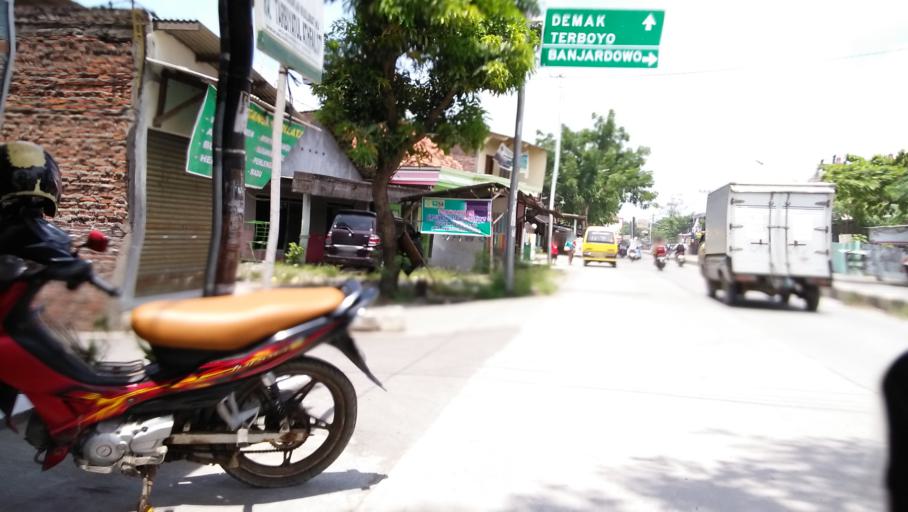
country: ID
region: Central Java
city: Semarang
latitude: -6.9711
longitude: 110.4813
